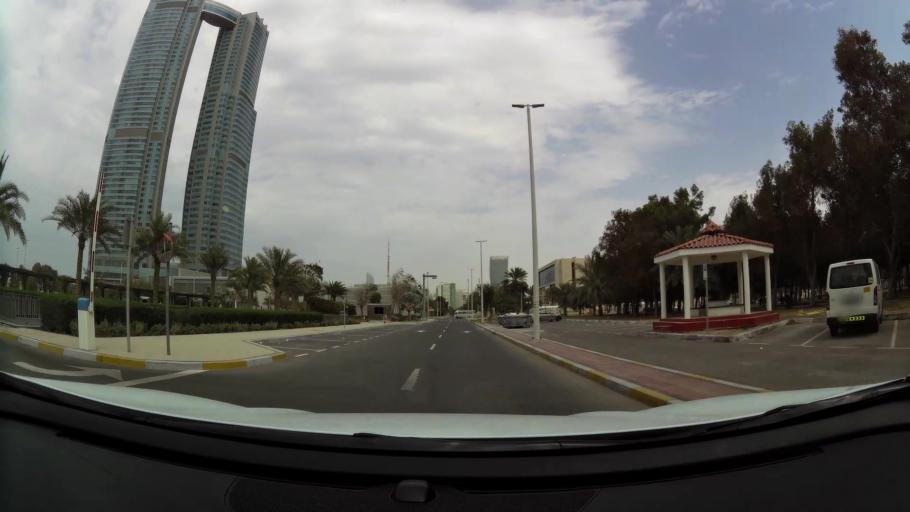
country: AE
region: Abu Dhabi
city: Abu Dhabi
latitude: 24.4614
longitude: 54.3271
